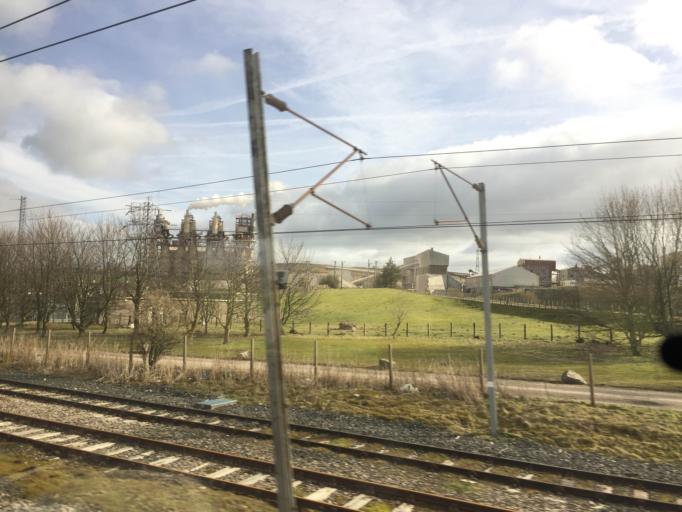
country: GB
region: England
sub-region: Cumbria
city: Penrith
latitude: 54.5127
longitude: -2.6687
